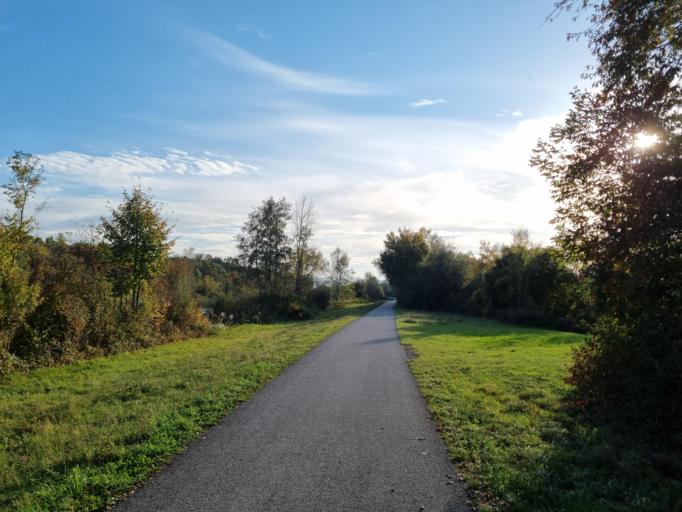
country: AT
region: Lower Austria
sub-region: Politischer Bezirk Sankt Polten
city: Wilhelmsburg
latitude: 48.1411
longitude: 15.6379
